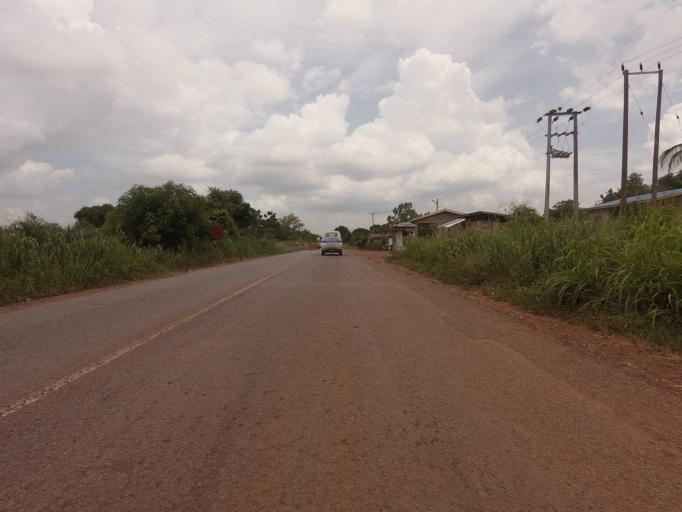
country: GH
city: Akropong
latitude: 6.2642
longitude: 0.1359
